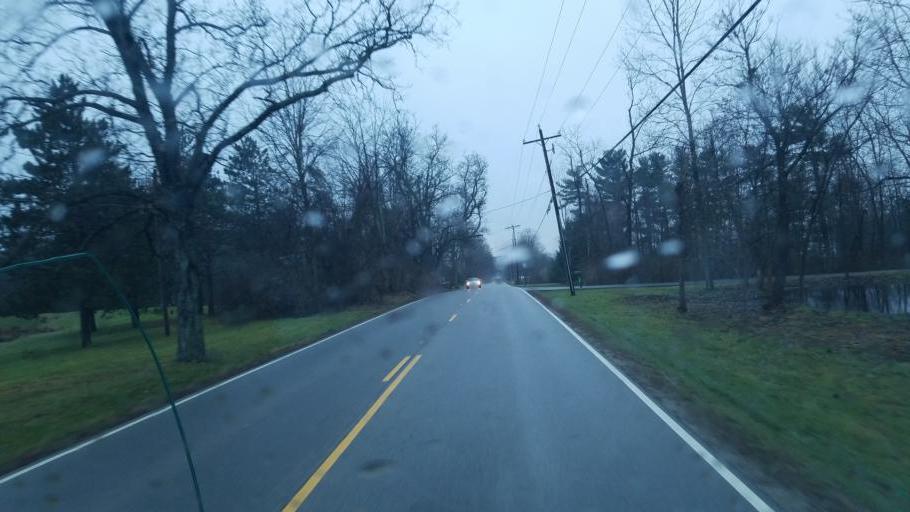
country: US
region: Ohio
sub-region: Delaware County
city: Lewis Center
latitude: 40.1954
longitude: -83.0370
